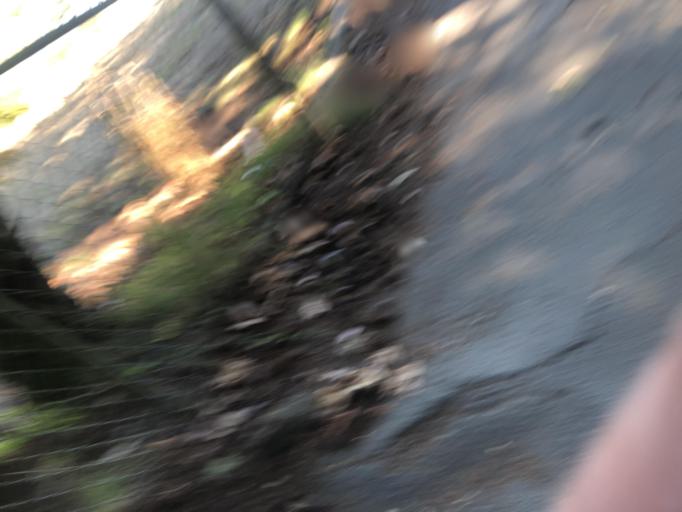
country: CA
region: British Columbia
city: North Saanich
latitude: 48.6057
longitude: -123.5217
